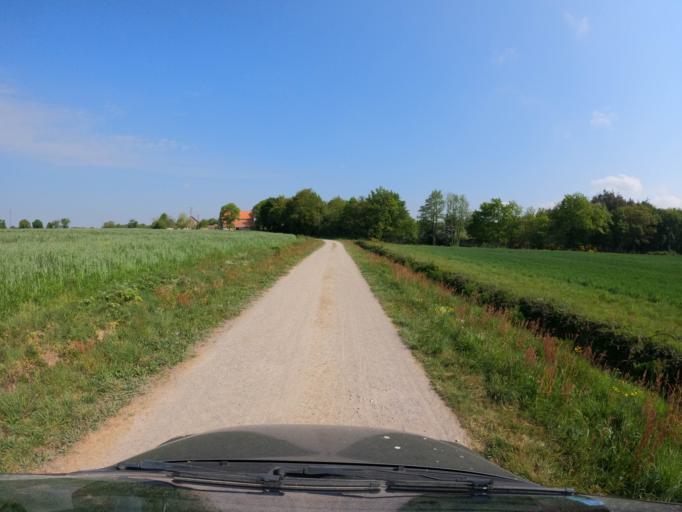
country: FR
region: Pays de la Loire
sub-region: Departement de la Vendee
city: Treize-Septiers
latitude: 47.0011
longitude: -1.2427
